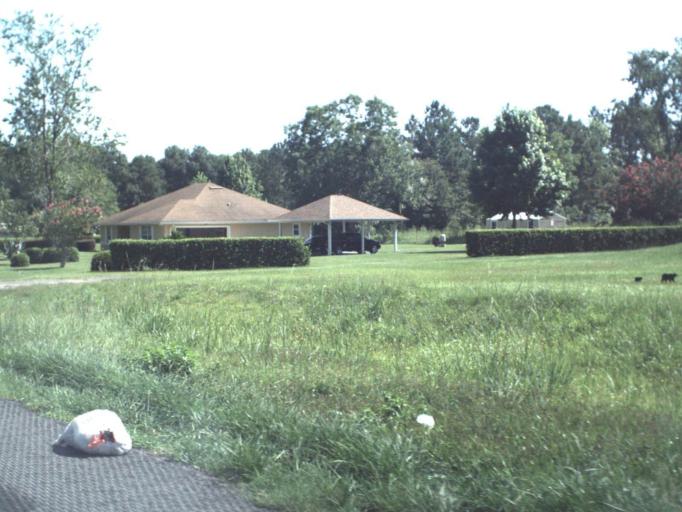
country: US
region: Florida
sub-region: Alachua County
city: Alachua
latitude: 29.8161
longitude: -82.3868
